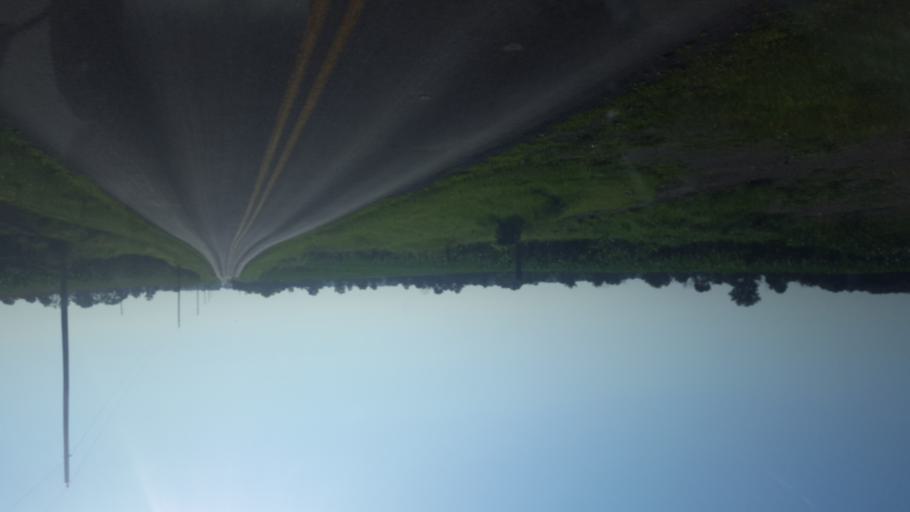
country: US
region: Ohio
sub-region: Hardin County
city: Kenton
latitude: 40.5613
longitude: -83.5634
